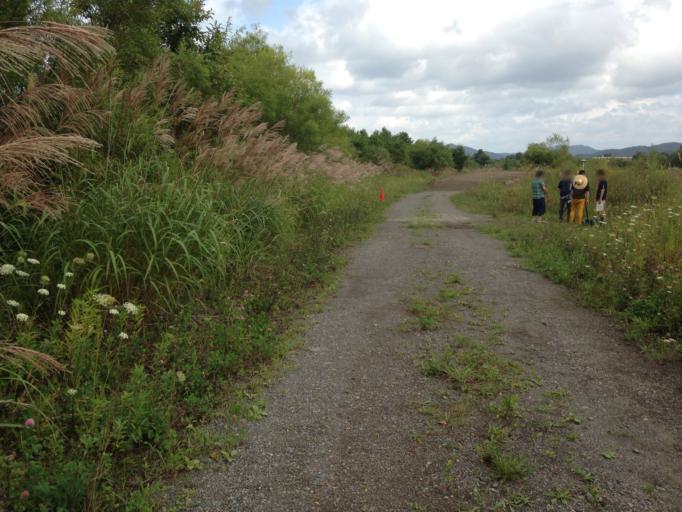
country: JP
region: Hokkaido
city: Tobetsu
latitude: 43.2572
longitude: 141.5292
